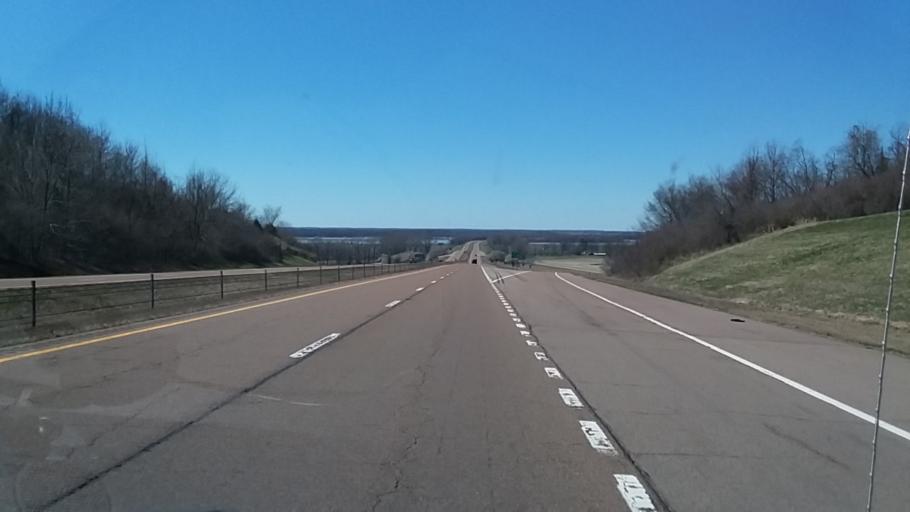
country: US
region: Tennessee
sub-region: Dyer County
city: Dyersburg
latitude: 36.0748
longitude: -89.4897
